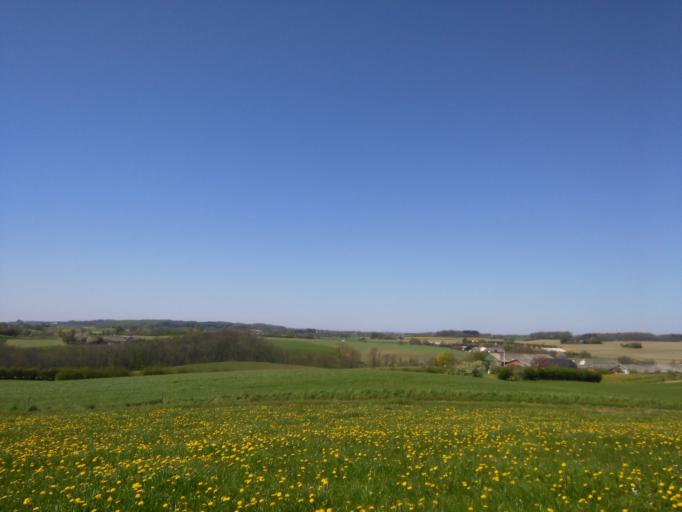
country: DK
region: Central Jutland
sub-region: Odder Kommune
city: Odder
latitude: 55.8988
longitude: 10.0354
